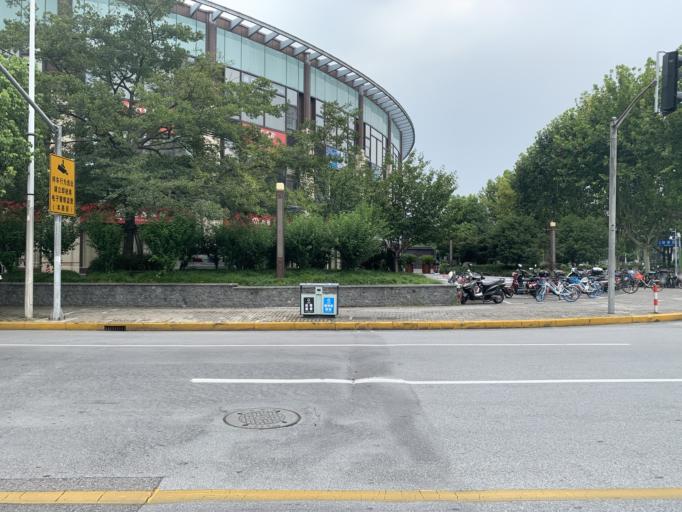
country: CN
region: Shanghai Shi
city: Huamu
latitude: 31.2273
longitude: 121.5543
